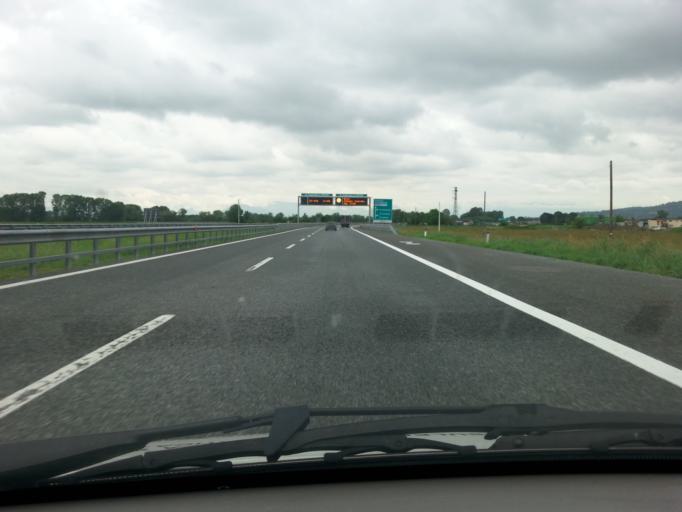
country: IT
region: Piedmont
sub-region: Provincia di Torino
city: La Loggia
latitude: 44.9588
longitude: 7.7083
